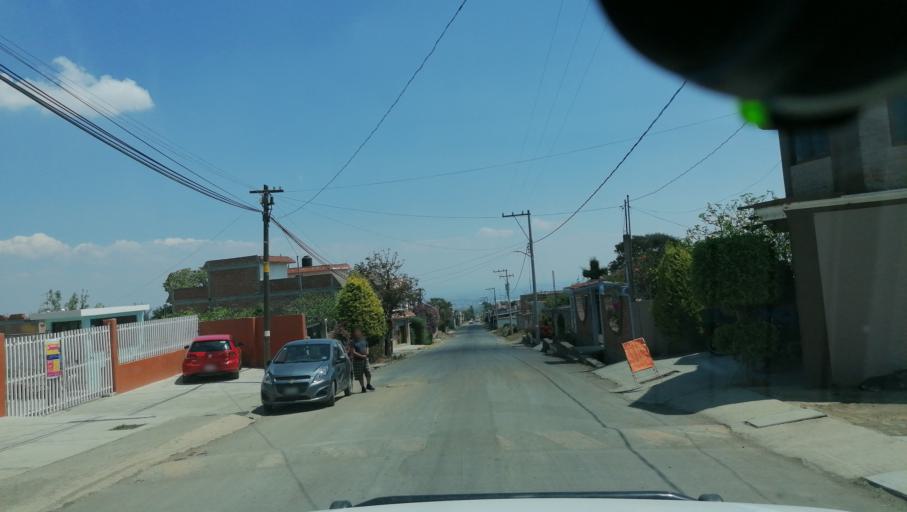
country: MX
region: Puebla
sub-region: Chiautzingo
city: San Nicolas Zecalacoayan
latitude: 19.1744
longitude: -98.4945
